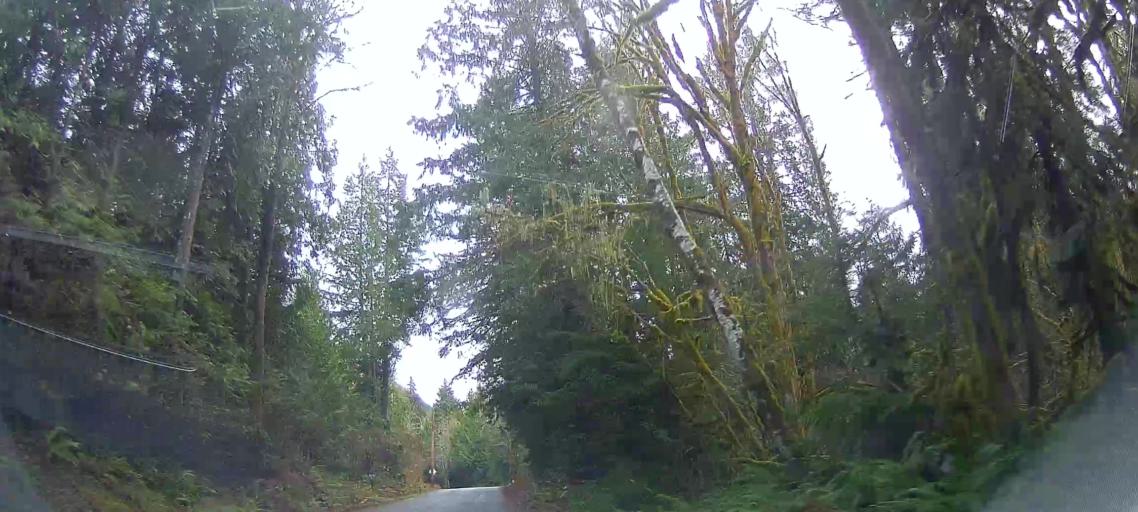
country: US
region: Washington
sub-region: Snohomish County
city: Darrington
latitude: 48.5305
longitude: -121.3994
